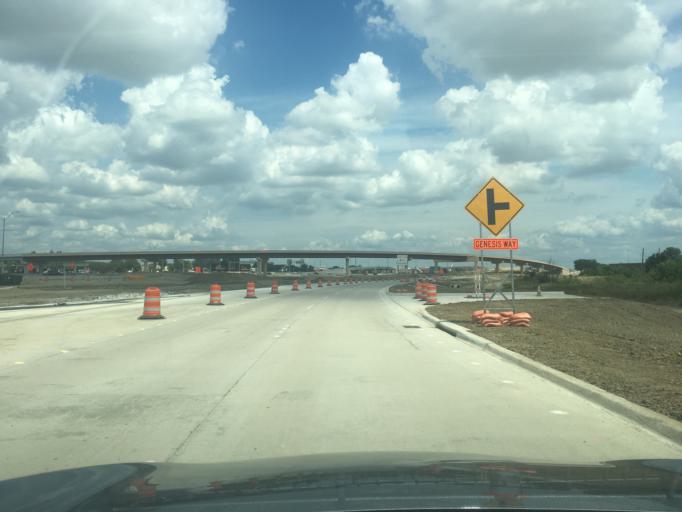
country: US
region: Texas
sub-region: Dallas County
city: Coppell
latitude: 32.9588
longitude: -97.0387
